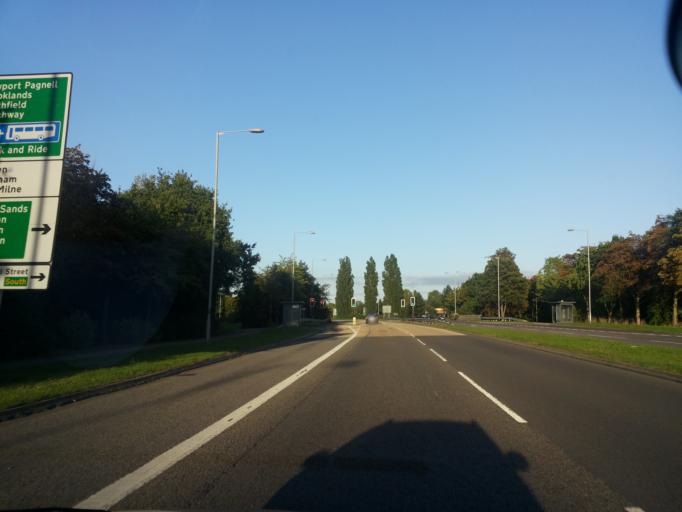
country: GB
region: England
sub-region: Milton Keynes
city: Broughton
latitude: 52.0476
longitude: -0.7112
